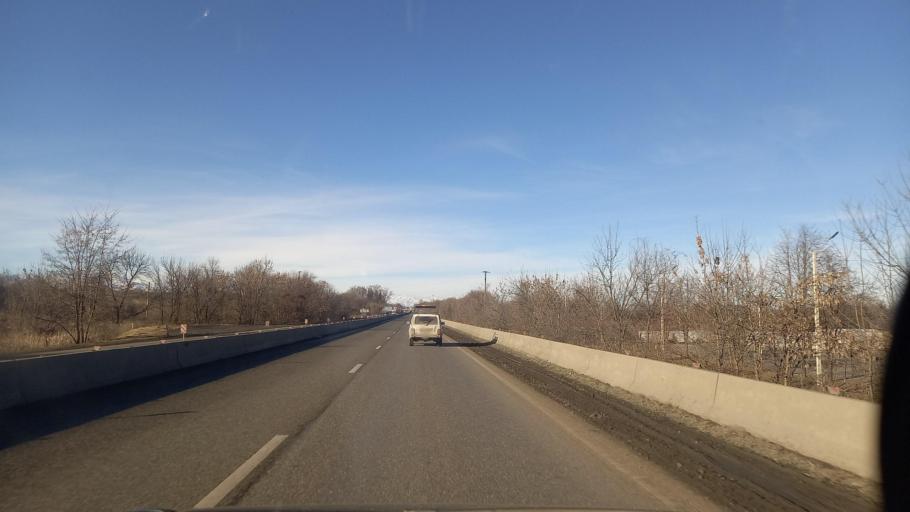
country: RU
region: North Ossetia
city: Gizel'
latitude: 43.0282
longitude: 44.5968
